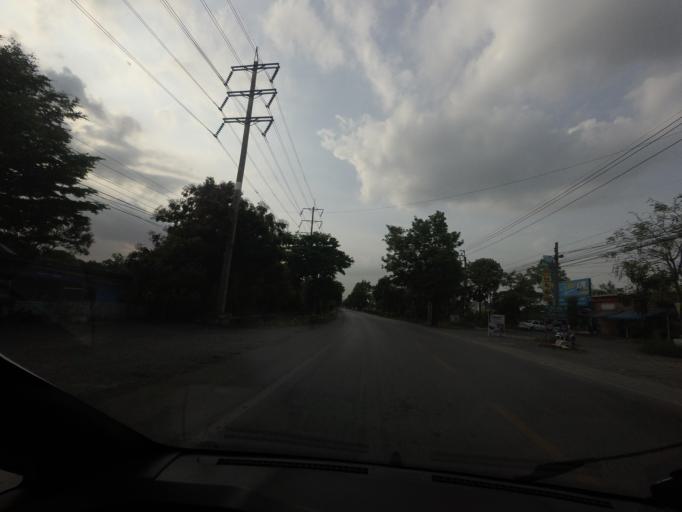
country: TH
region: Bangkok
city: Nong Chok
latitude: 13.8912
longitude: 100.8636
